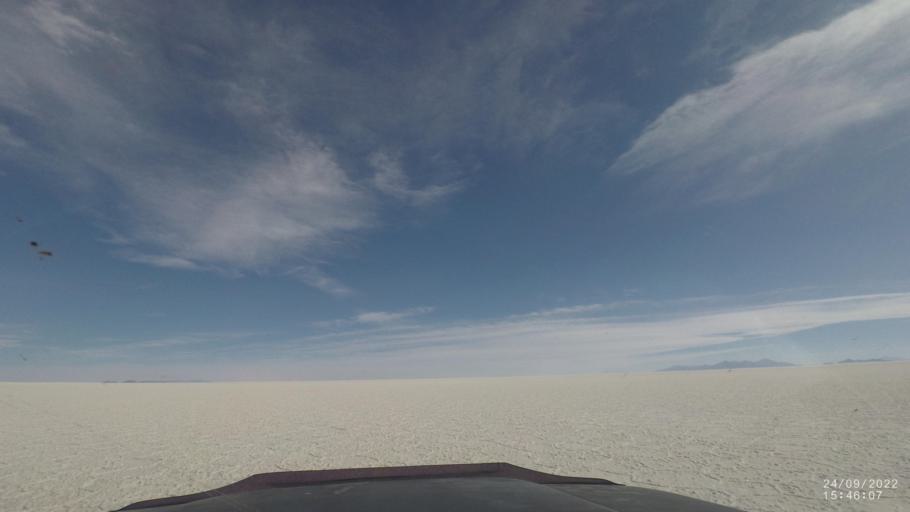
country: BO
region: Potosi
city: Colchani
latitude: -20.2635
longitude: -67.2219
